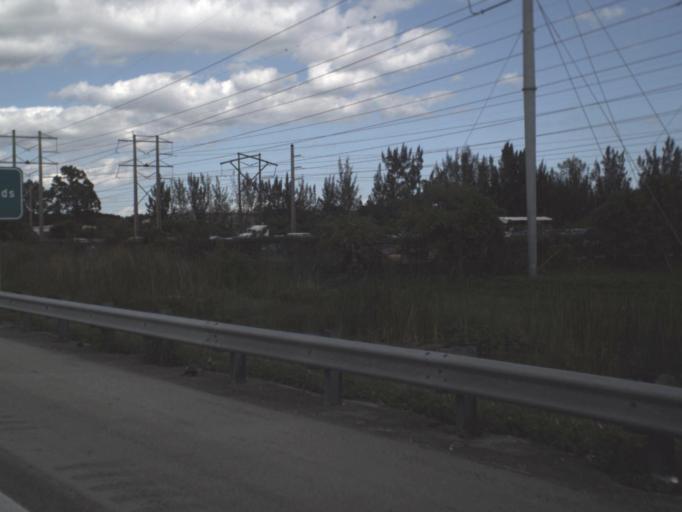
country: US
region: Florida
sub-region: Broward County
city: Davie
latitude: 26.0558
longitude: -80.2149
